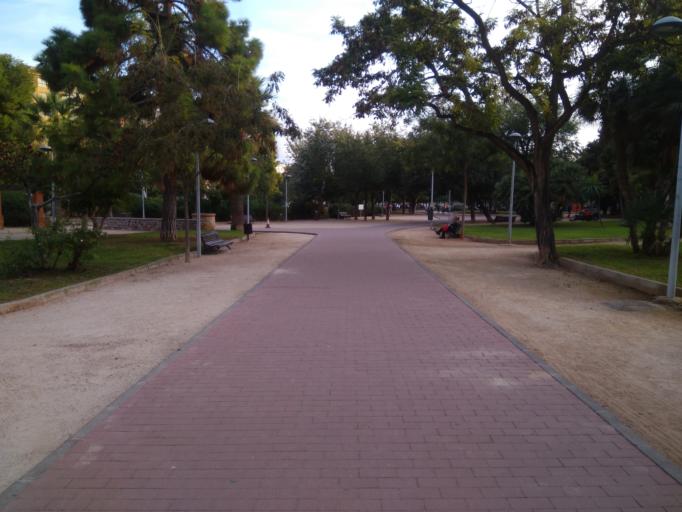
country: ES
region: Valencia
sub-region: Provincia de Castello
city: Castello de la Plana
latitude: 39.9789
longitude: -0.0380
